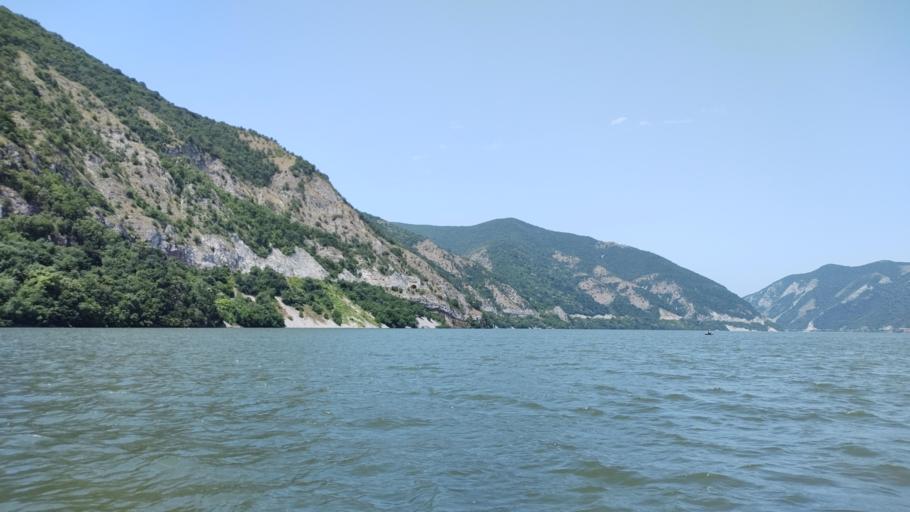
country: RO
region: Mehedinti
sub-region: Comuna Svinita
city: Svinita
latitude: 44.5572
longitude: 22.0299
